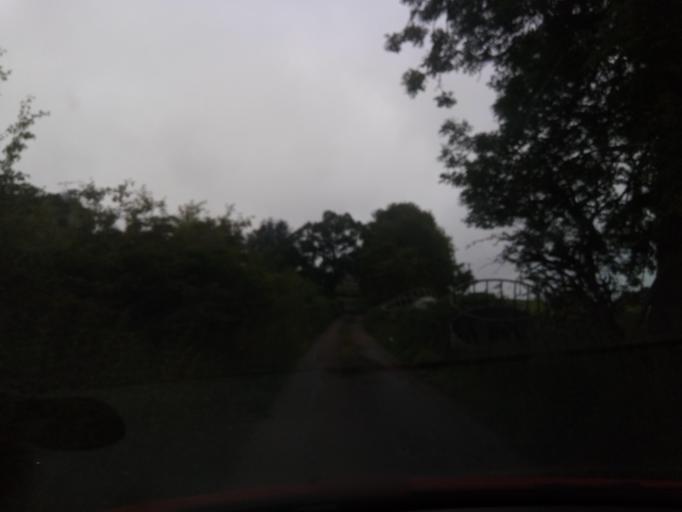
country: GB
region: England
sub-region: Northumberland
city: Otterburn
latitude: 55.2765
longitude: -2.0931
